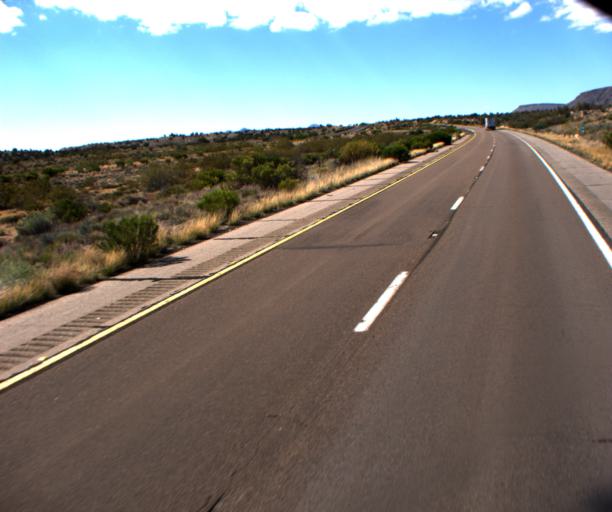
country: US
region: Arizona
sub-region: Mohave County
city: New Kingman-Butler
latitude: 35.1277
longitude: -113.6665
